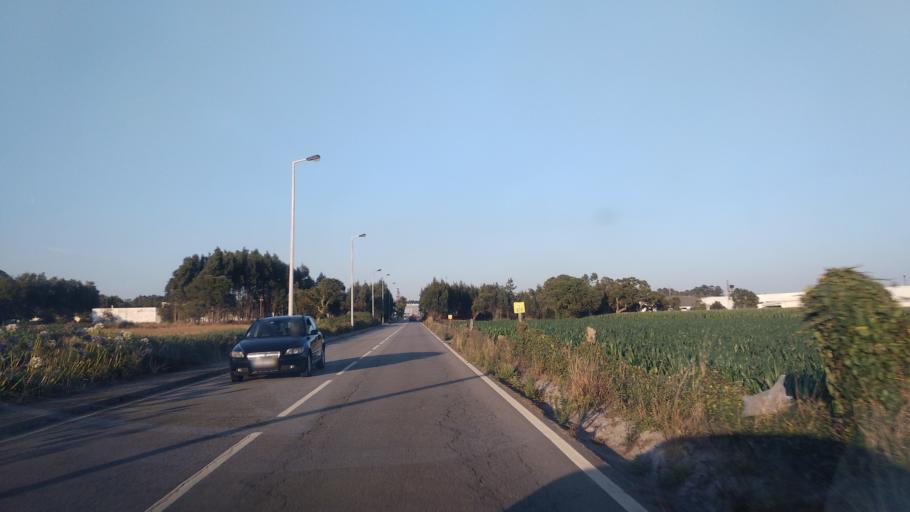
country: PT
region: Braga
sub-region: Esposende
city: Esposende
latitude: 41.5319
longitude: -8.7692
